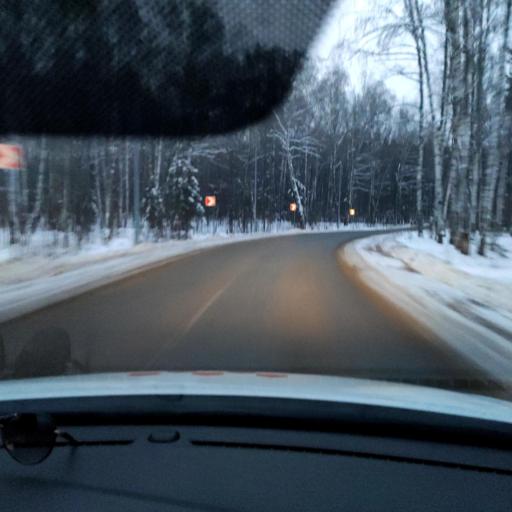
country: RU
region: Tatarstan
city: Vysokaya Gora
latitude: 55.9307
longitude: 49.1568
